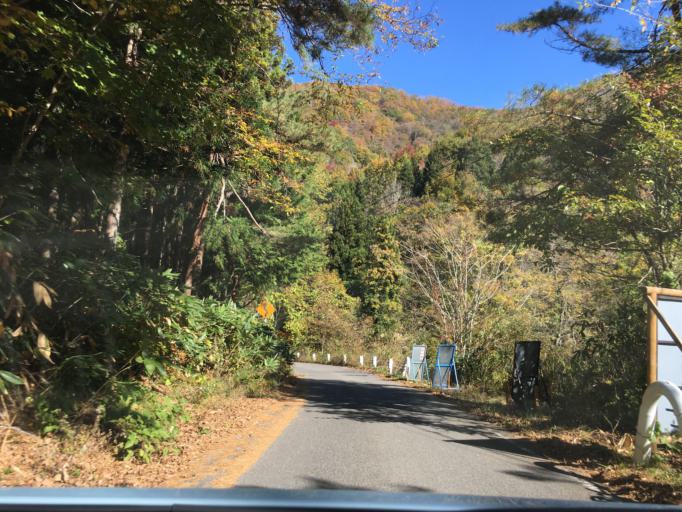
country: JP
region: Fukushima
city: Inawashiro
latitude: 37.4086
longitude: 139.9951
